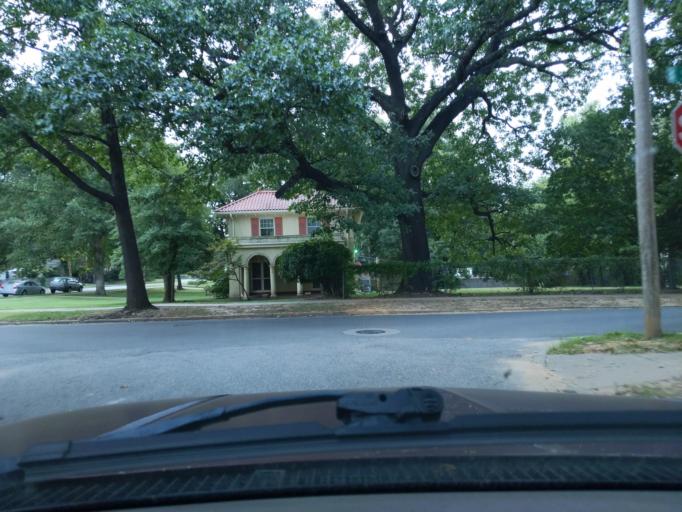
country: US
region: Oklahoma
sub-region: Tulsa County
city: Tulsa
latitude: 36.1368
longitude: -95.9709
